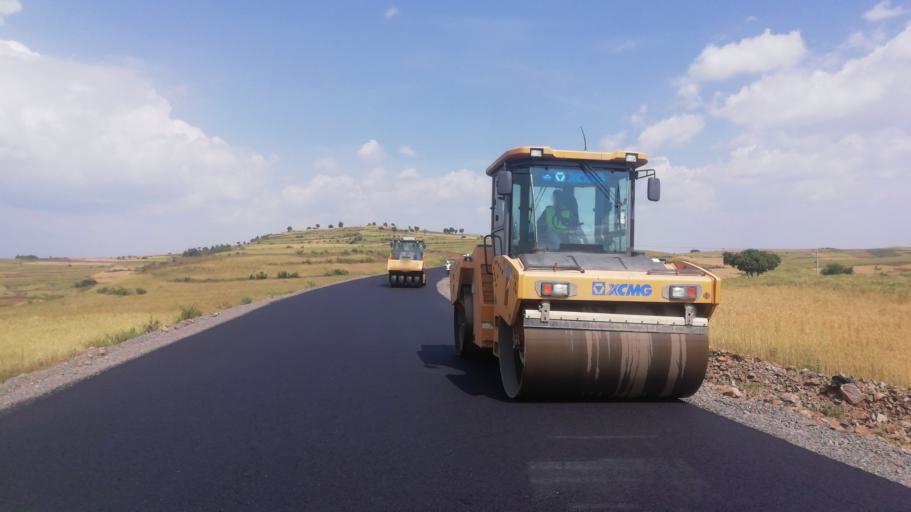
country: ET
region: Amhara
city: Addiet Canna
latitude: 11.3718
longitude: 37.8741
